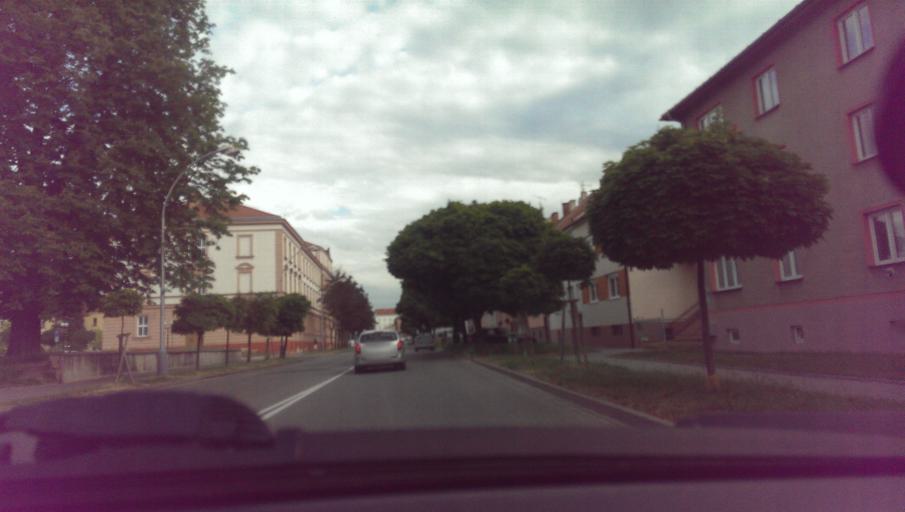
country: CZ
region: Zlin
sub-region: Okres Kromeriz
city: Kromeriz
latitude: 49.2927
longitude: 17.3914
